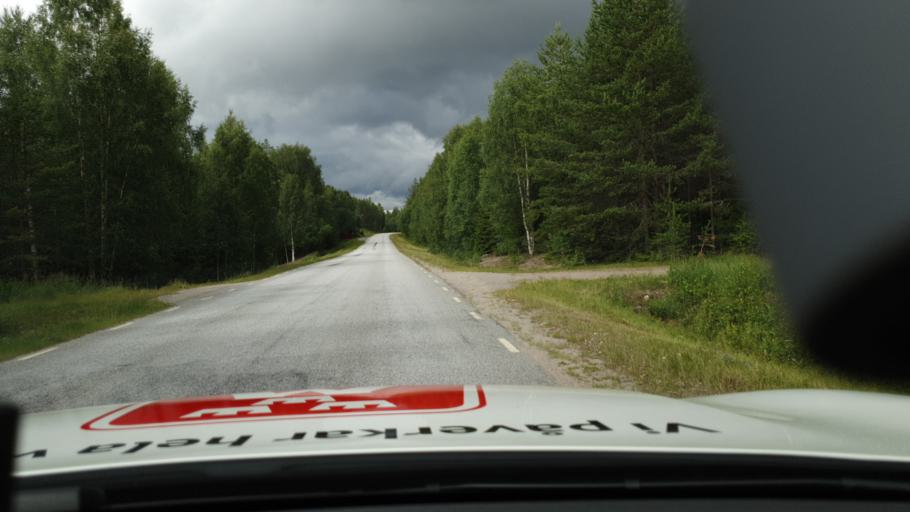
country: SE
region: Norrbotten
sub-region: Pitea Kommun
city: Rosvik
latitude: 65.4134
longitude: 21.7356
